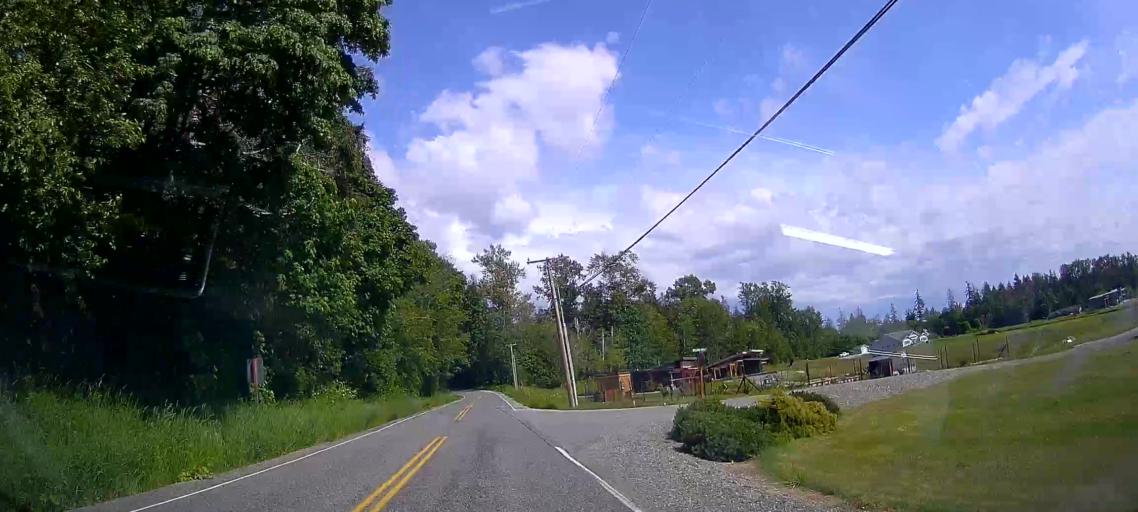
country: US
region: Washington
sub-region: Skagit County
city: Burlington
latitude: 48.5709
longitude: -122.3922
